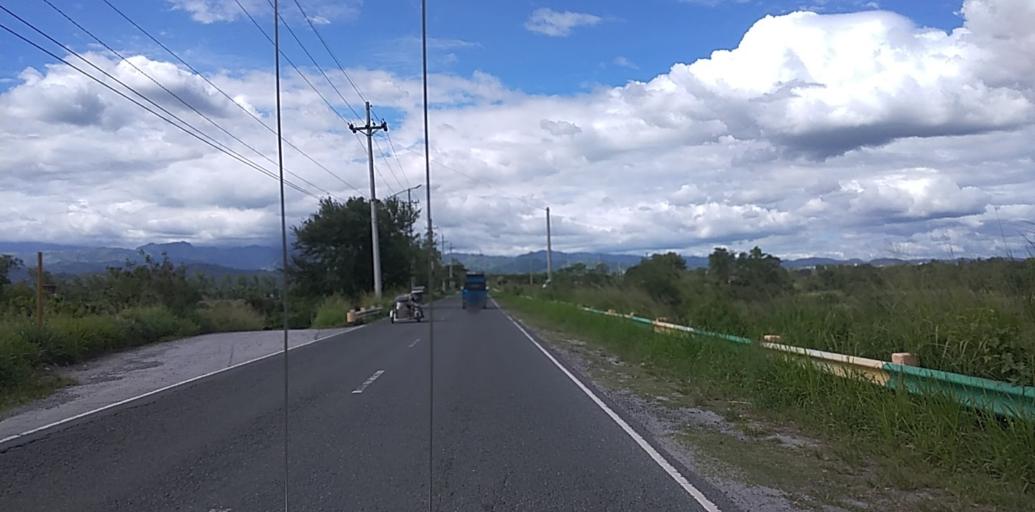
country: PH
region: Central Luzon
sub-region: Province of Pampanga
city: Porac
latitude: 15.0857
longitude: 120.5419
